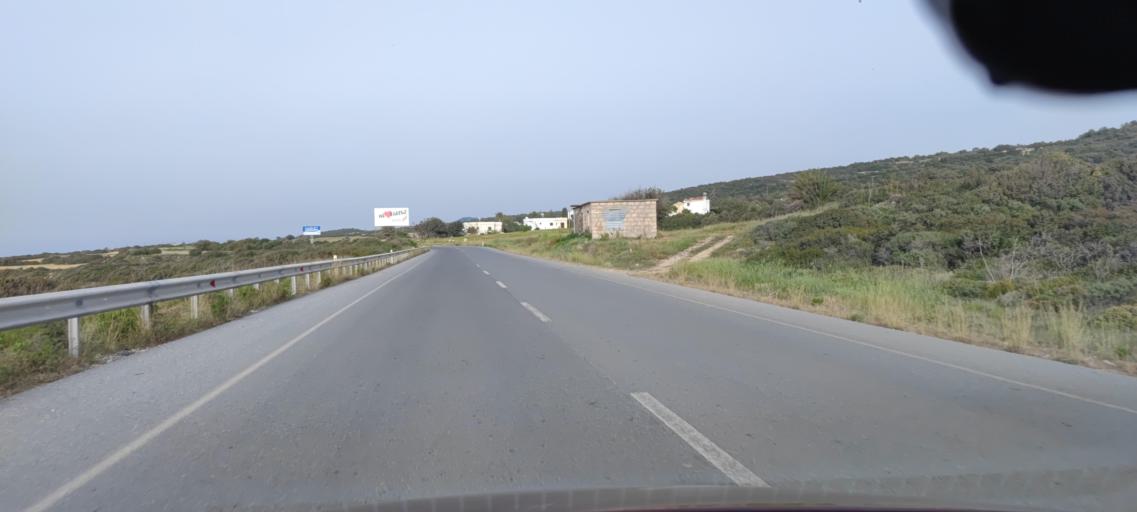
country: CY
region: Ammochostos
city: Leonarisso
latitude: 35.5585
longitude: 34.2365
